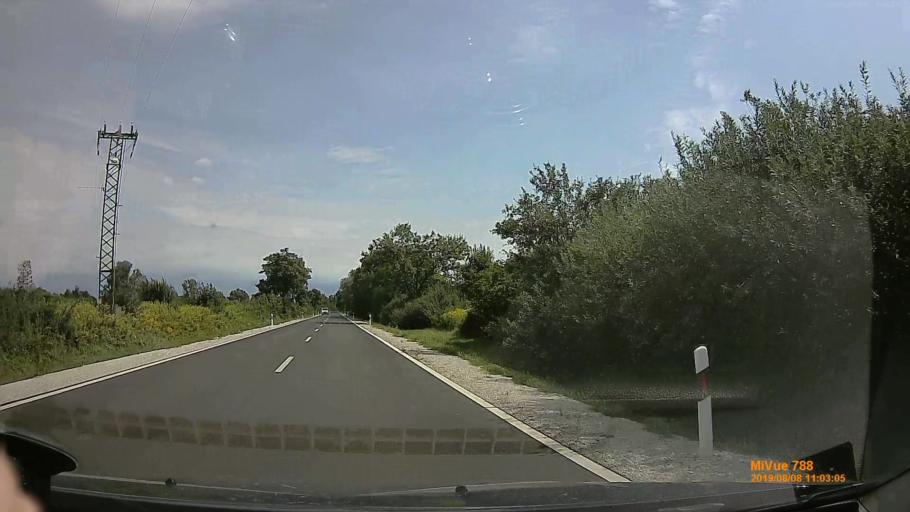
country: HU
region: Zala
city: Zalakomar
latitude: 46.5277
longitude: 17.1570
